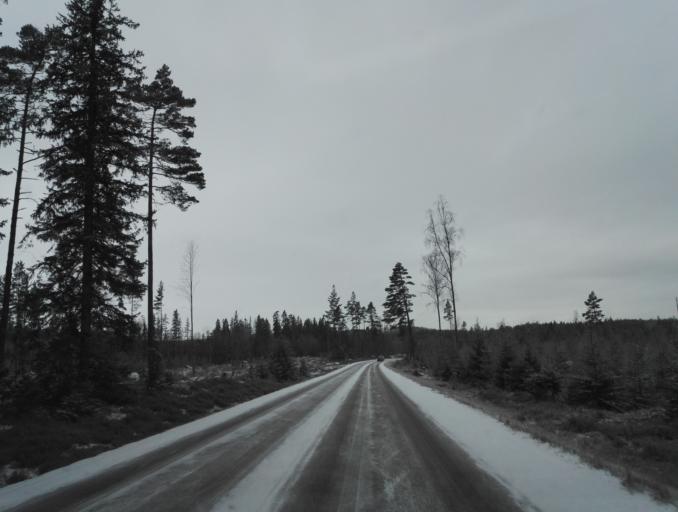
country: SE
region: Kronoberg
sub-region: Lessebo Kommun
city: Lessebo
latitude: 56.8111
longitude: 15.3704
